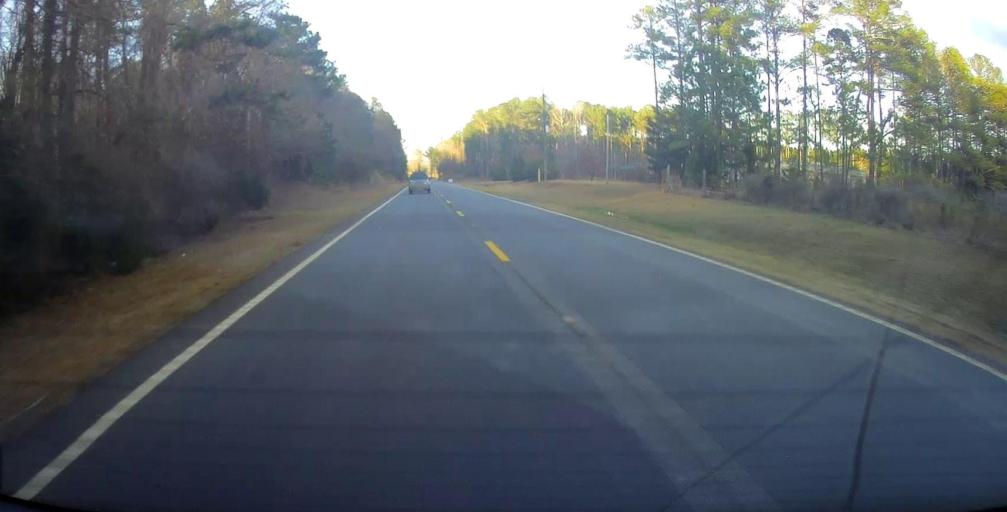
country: US
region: Georgia
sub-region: Talbot County
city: Sardis
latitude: 32.7001
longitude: -84.7001
